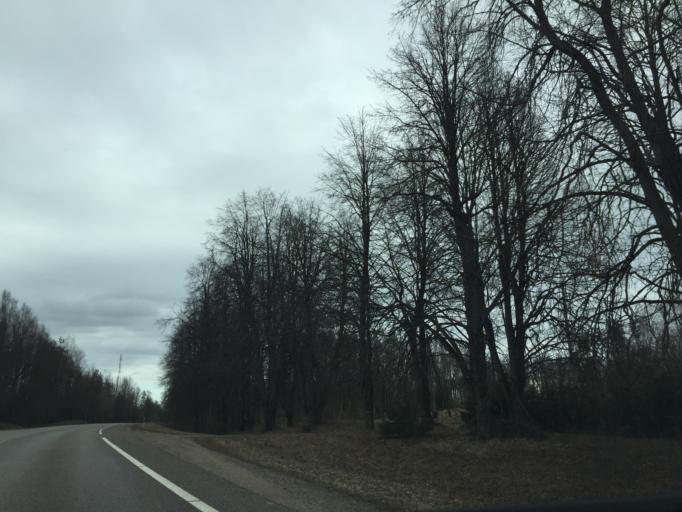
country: LV
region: Kraslavas Rajons
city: Kraslava
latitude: 55.9010
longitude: 27.1182
